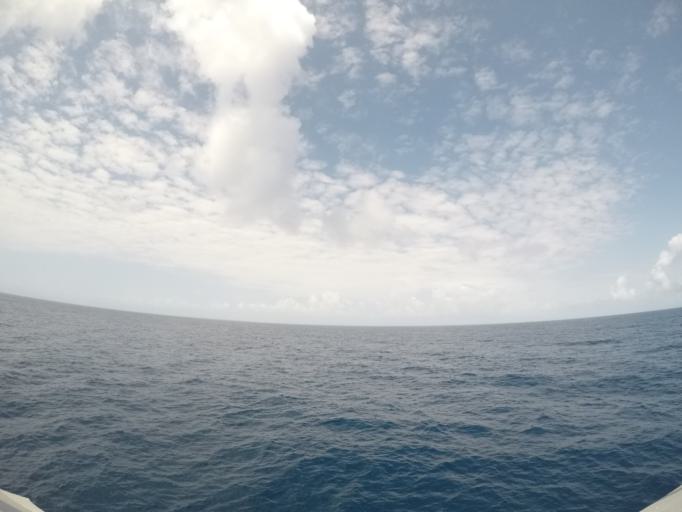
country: TZ
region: Zanzibar North
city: Nungwi
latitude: -5.5728
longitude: 39.3663
